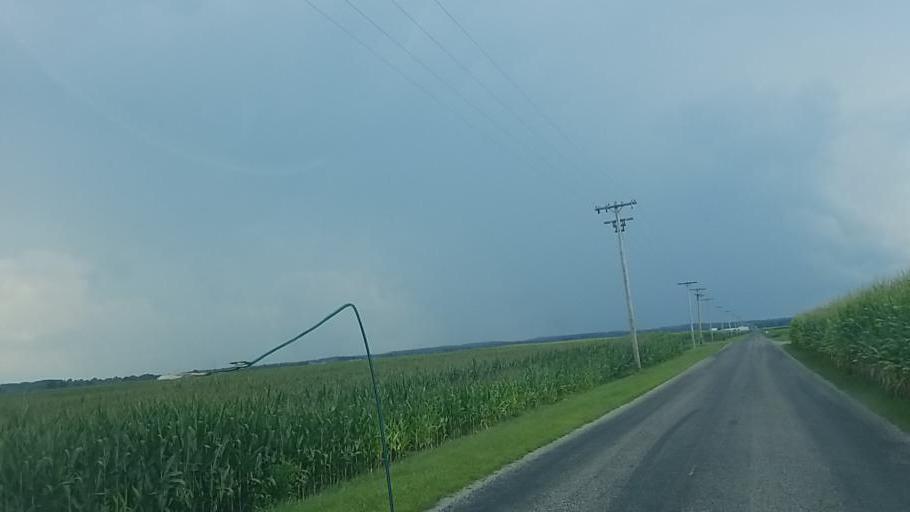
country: US
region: Ohio
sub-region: Medina County
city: Lodi
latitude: 41.0239
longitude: -82.0180
